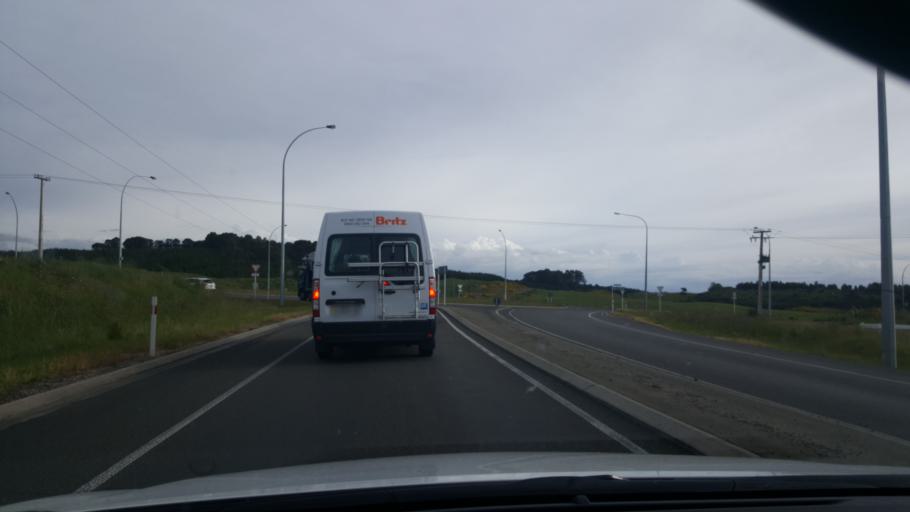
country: NZ
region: Waikato
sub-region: Taupo District
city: Taupo
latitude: -38.7035
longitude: 176.1120
